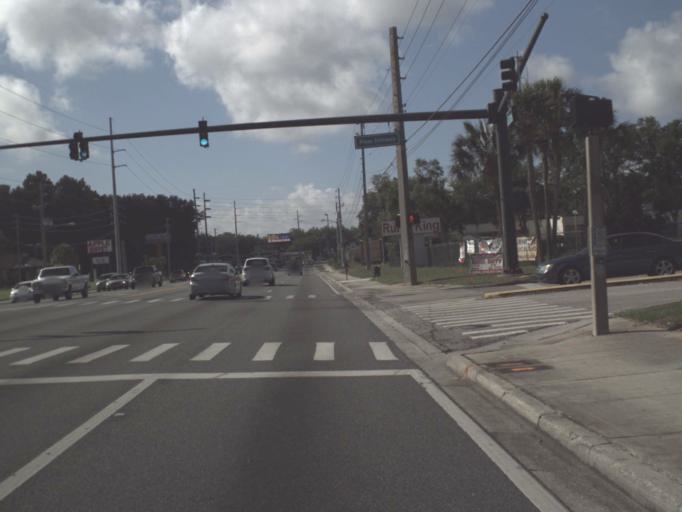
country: US
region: Florida
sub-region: Lake County
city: Leesburg
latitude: 28.8343
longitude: -81.8896
